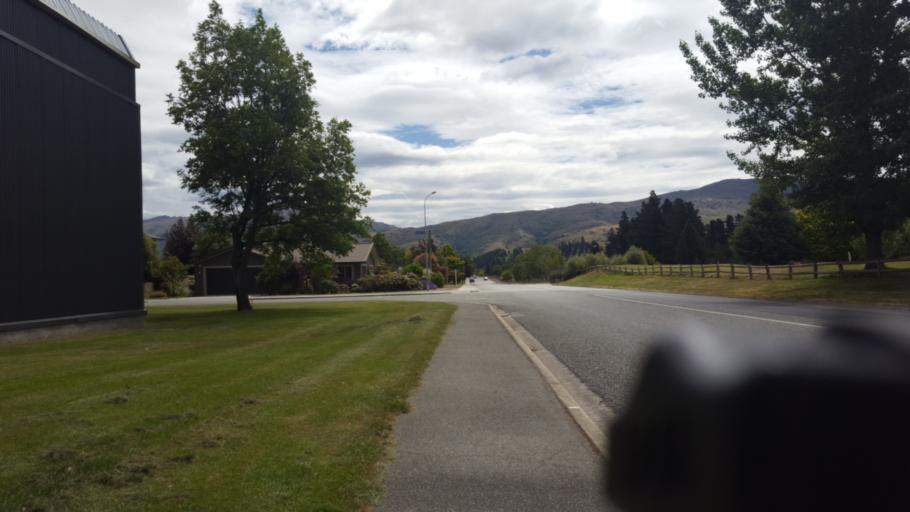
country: NZ
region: Otago
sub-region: Queenstown-Lakes District
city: Wanaka
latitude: -45.0414
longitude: 169.2086
